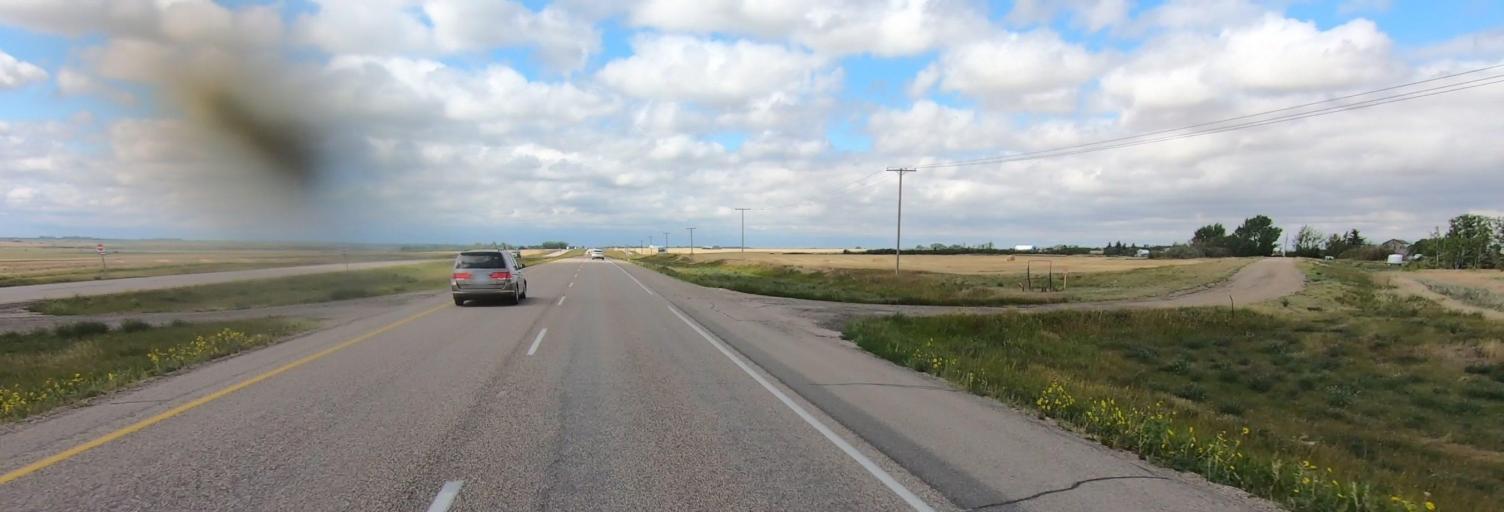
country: CA
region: Saskatchewan
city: Moose Jaw
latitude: 50.4361
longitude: -105.7589
